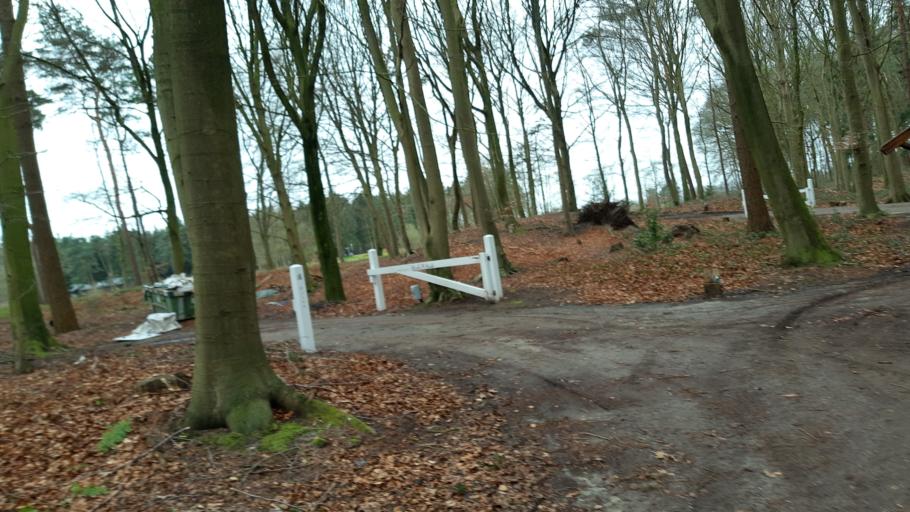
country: NL
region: Drenthe
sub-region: Gemeente Assen
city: Assen
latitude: 52.8521
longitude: 6.5905
